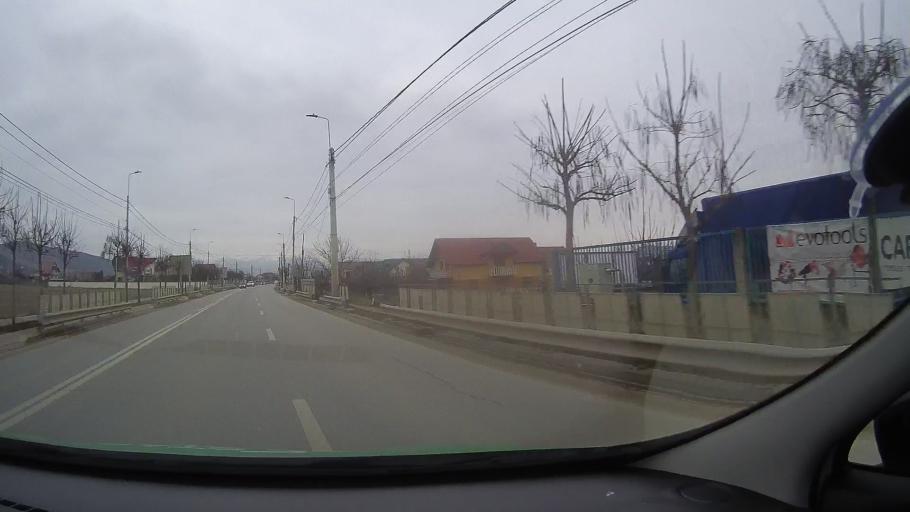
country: RO
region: Alba
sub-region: Municipiul Alba Iulia
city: Micesti
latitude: 46.0957
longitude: 23.5530
